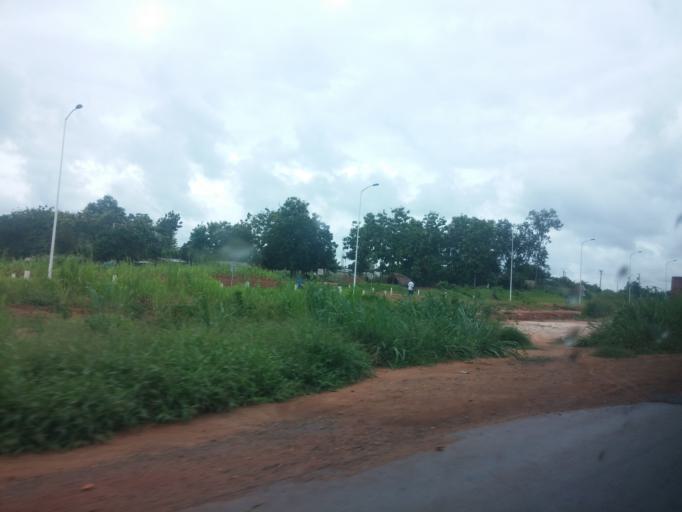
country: TG
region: Maritime
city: Tsevie
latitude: 6.3457
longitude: 1.2137
